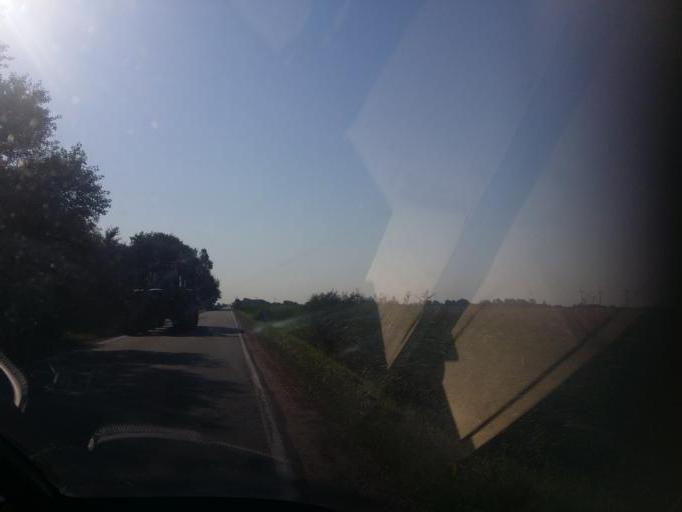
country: DE
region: Schleswig-Holstein
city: Emmelsbull-Horsbull
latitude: 54.8089
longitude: 8.7044
